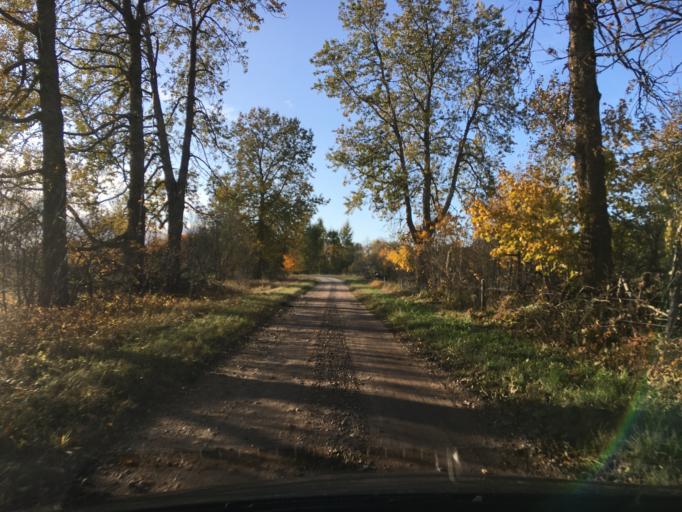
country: EE
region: Laeaene
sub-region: Lihula vald
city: Lihula
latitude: 58.5652
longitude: 23.7872
